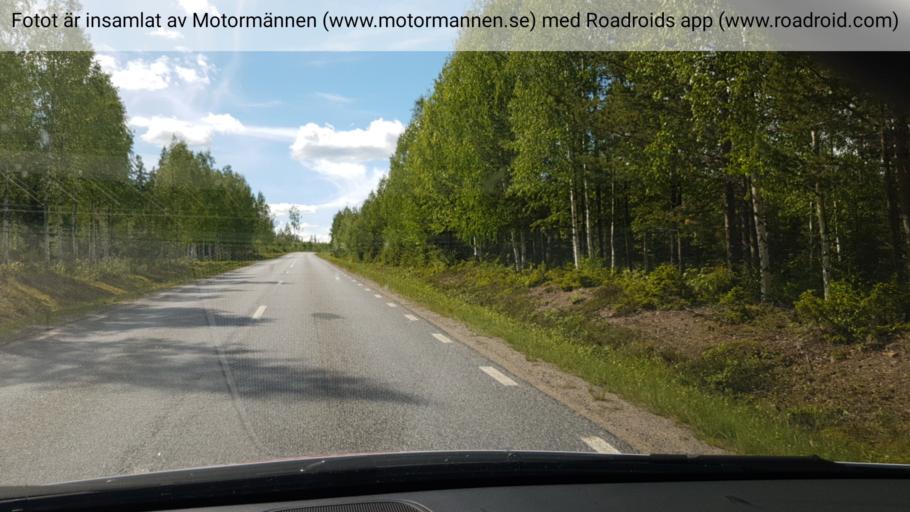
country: SE
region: Vaesterbotten
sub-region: Skelleftea Kommun
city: Burtraesk
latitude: 64.5062
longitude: 20.5544
